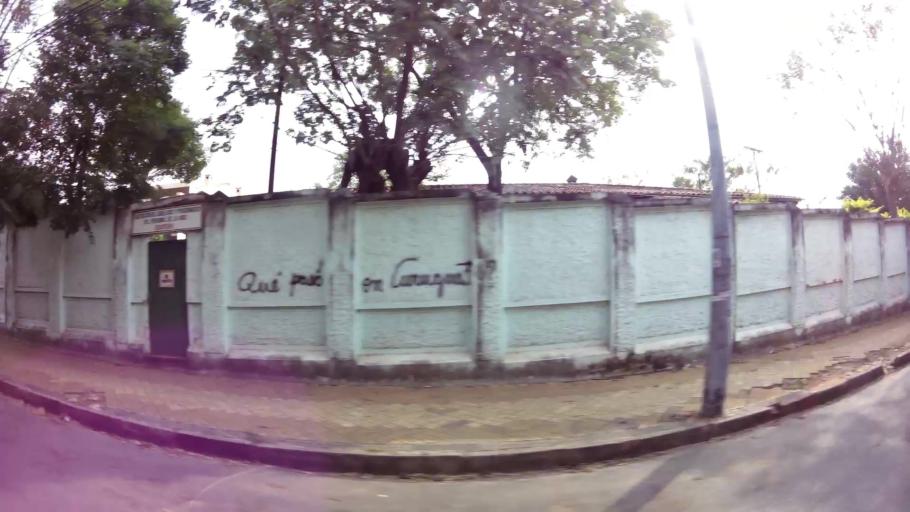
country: PY
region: Asuncion
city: Asuncion
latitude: -25.2892
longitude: -57.6140
